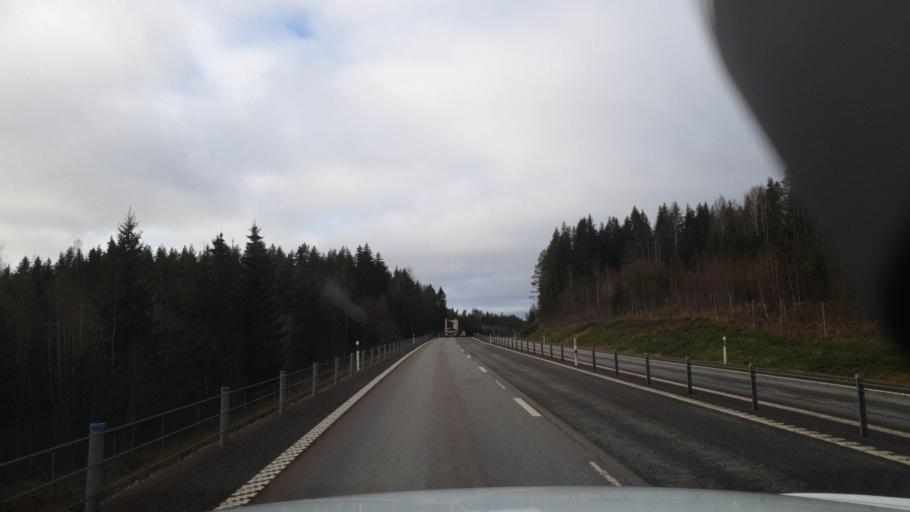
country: SE
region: Vaermland
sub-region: Arvika Kommun
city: Arvika
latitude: 59.6438
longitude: 12.7331
